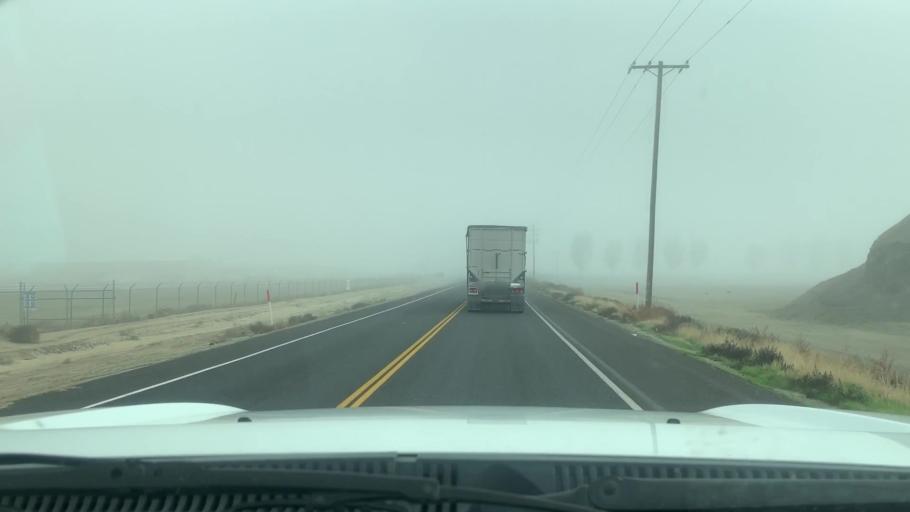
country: US
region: California
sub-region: Kern County
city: Buttonwillow
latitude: 35.4994
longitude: -119.5495
